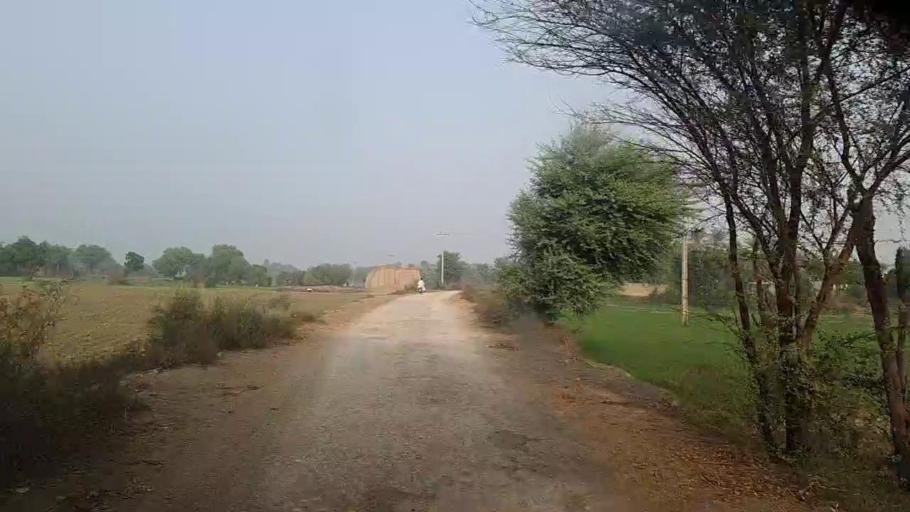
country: PK
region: Sindh
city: Bozdar
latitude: 27.1431
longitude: 68.6666
